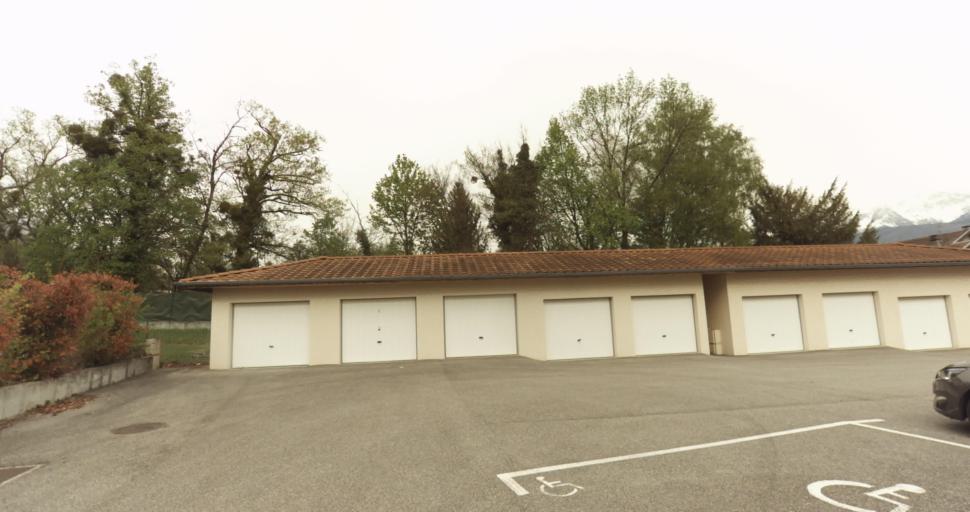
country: FR
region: Rhone-Alpes
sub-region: Departement de l'Isere
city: Montbonnot-Saint-Martin
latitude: 45.2322
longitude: 5.8181
